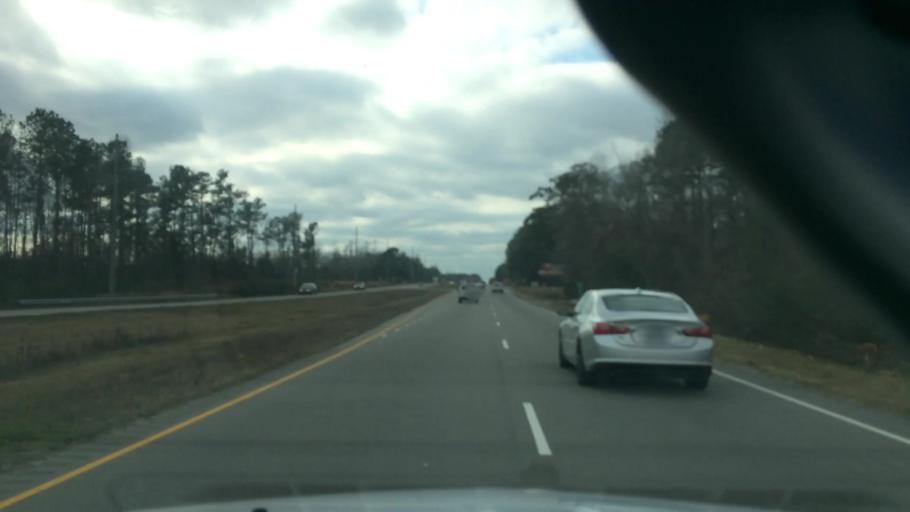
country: US
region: North Carolina
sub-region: Brunswick County
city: Shallotte
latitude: 33.9911
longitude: -78.3485
